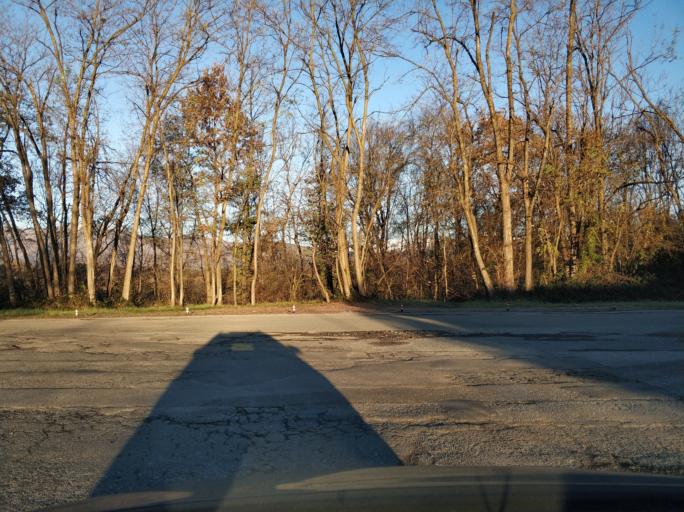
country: IT
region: Piedmont
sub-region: Provincia di Torino
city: Robassomero
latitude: 45.1775
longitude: 7.5871
